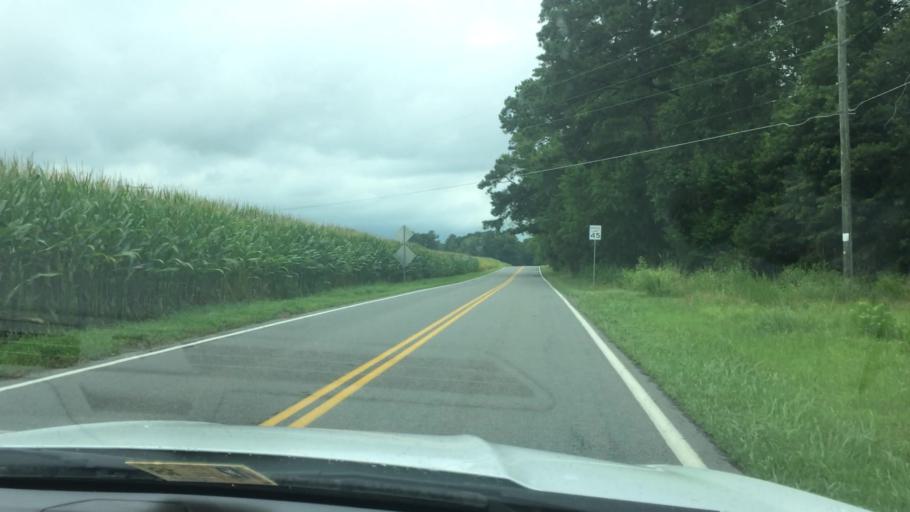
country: US
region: Virginia
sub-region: King William County
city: West Point
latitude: 37.5139
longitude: -76.8204
